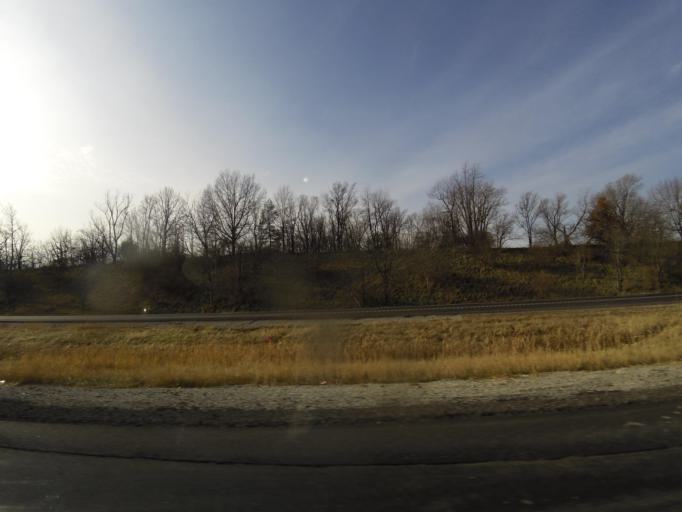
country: US
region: Illinois
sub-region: Macon County
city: Harristown
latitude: 39.8287
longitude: -89.0403
